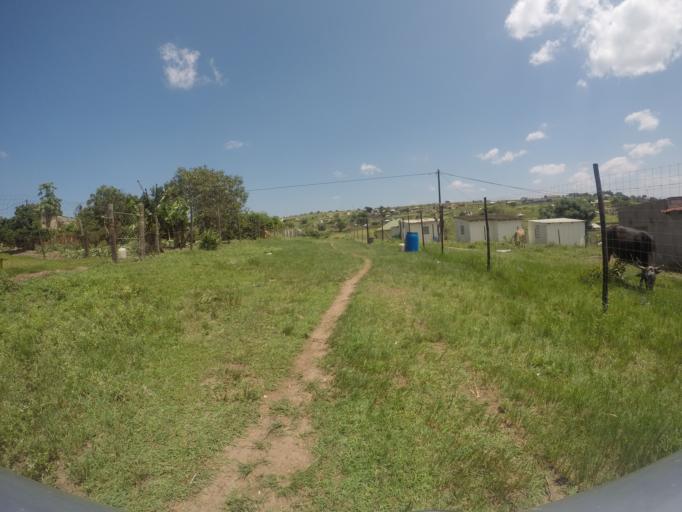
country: ZA
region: KwaZulu-Natal
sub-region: uThungulu District Municipality
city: Empangeni
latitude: -28.6060
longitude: 31.7382
